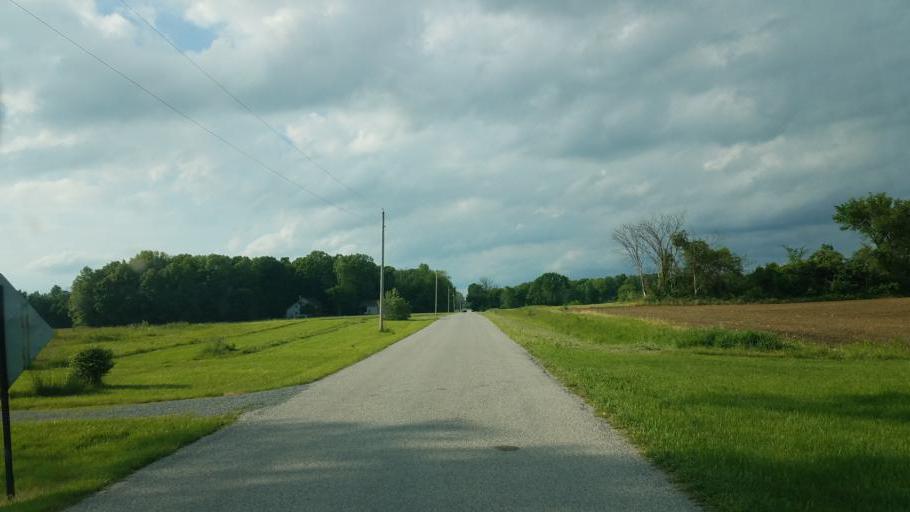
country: US
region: Ohio
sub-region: Knox County
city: Centerburg
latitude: 40.3757
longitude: -82.7624
